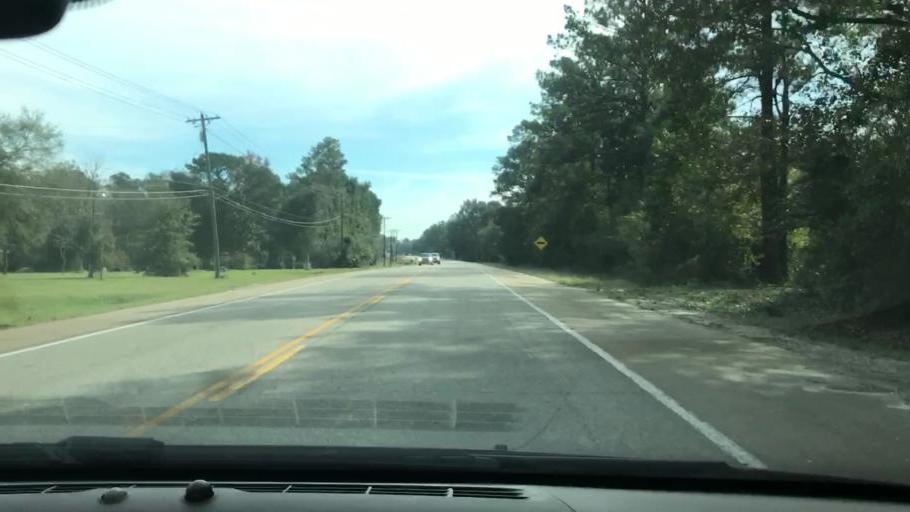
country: US
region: Louisiana
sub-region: Saint Tammany Parish
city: Pearl River
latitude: 30.4142
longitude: -89.7827
